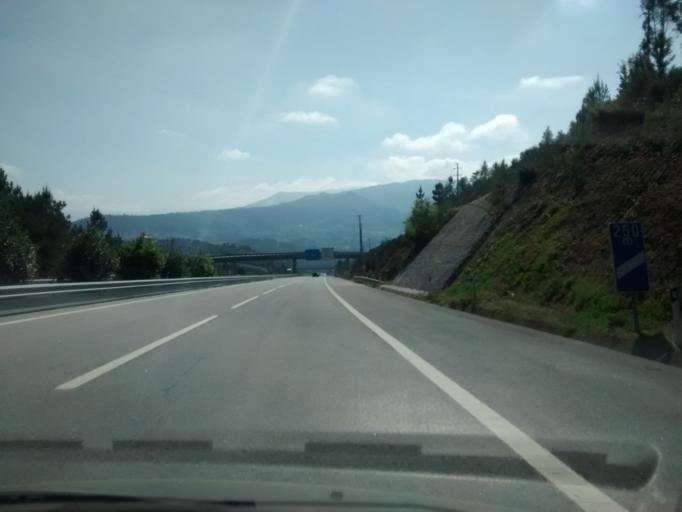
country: PT
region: Braga
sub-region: Cabeceiras de Basto
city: Cabeceiras de Basto
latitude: 41.4755
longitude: -7.9546
